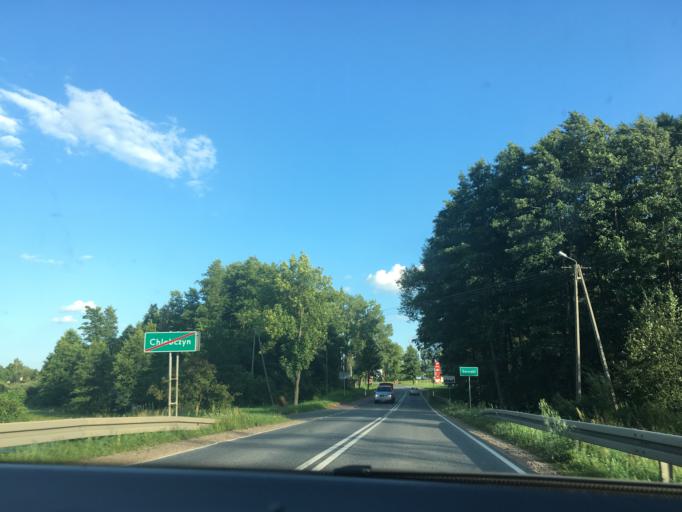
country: PL
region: Masovian Voivodeship
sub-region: Powiat losicki
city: Sarnaki
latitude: 52.3234
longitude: 22.8795
